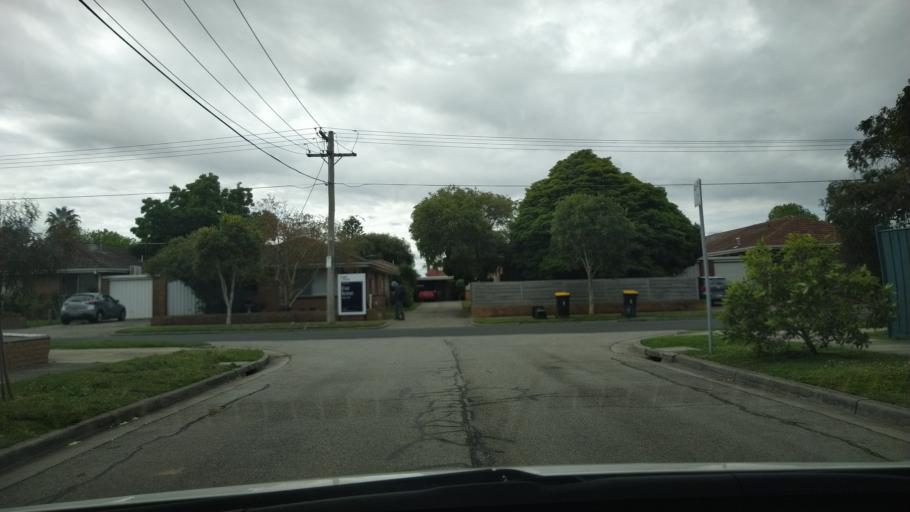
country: AU
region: Victoria
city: Highett
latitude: -37.9602
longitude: 145.0588
